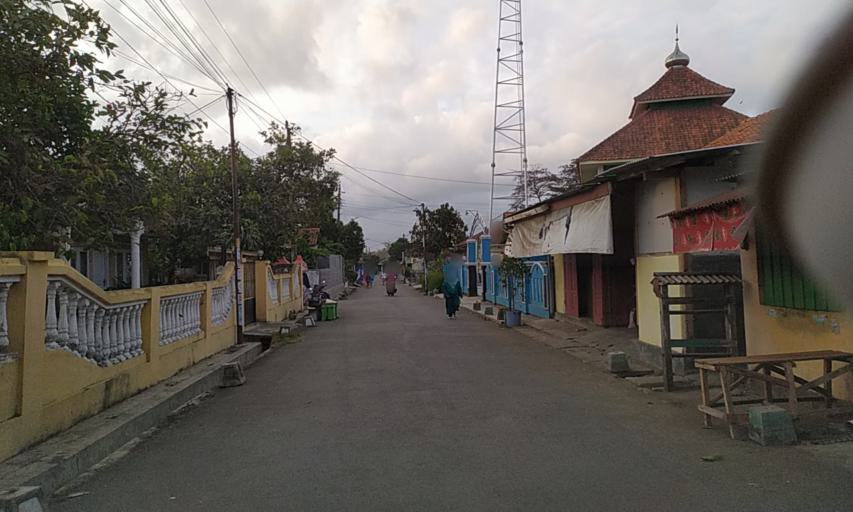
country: ID
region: Central Java
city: Rejanegara
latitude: -7.6658
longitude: 109.0393
